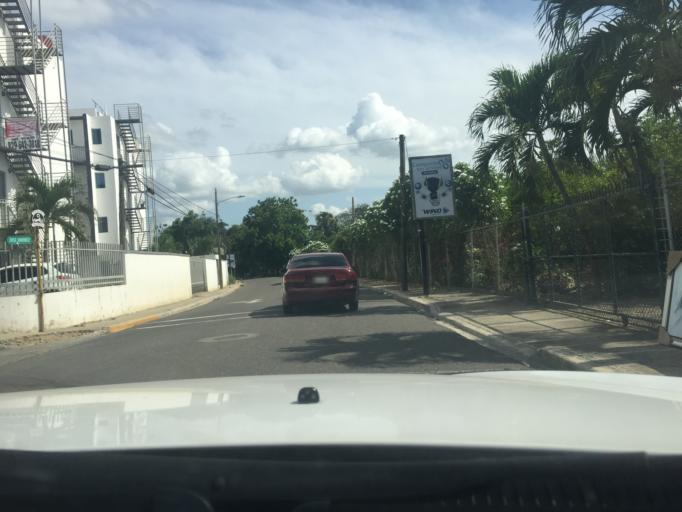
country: DO
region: Santiago
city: Tamboril
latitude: 19.4810
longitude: -70.6557
